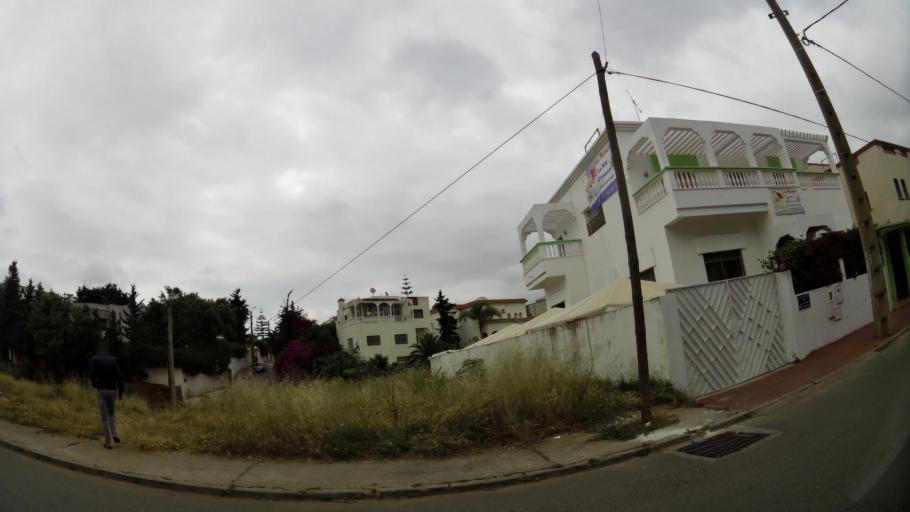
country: MA
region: Rabat-Sale-Zemmour-Zaer
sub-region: Rabat
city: Rabat
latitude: 33.9769
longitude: -6.8137
